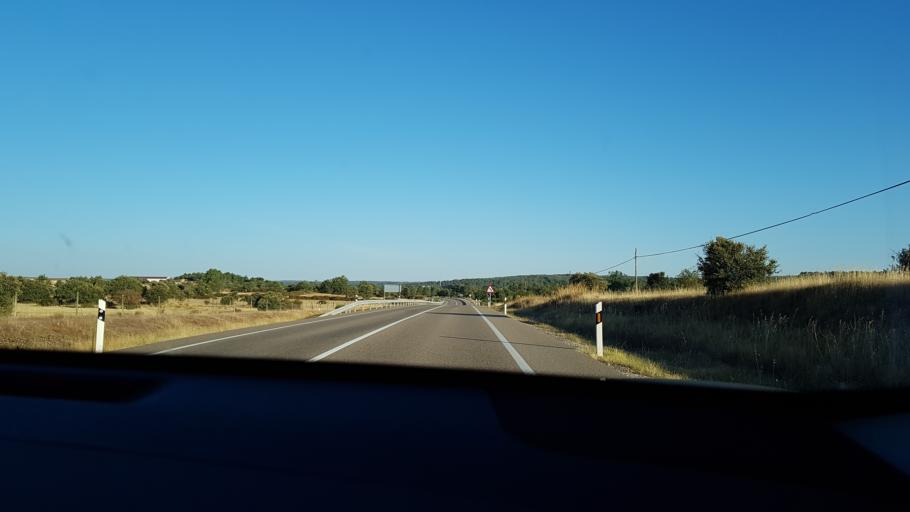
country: ES
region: Castille and Leon
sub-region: Provincia de Zamora
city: Samir de los Canos
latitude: 41.6519
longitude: -6.1753
